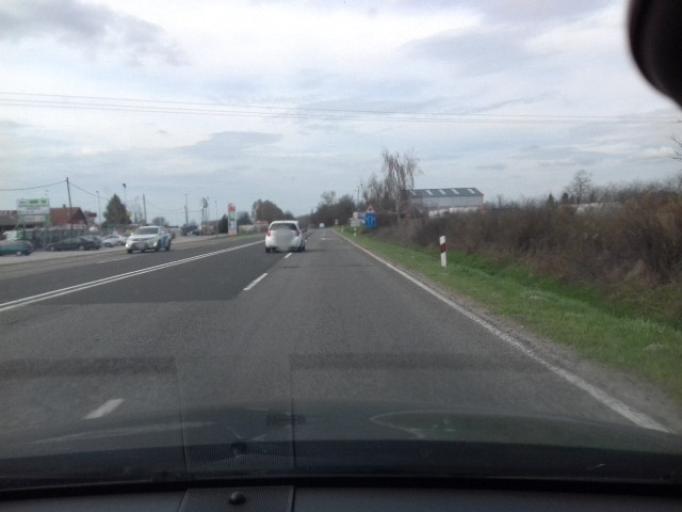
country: HU
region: Bacs-Kiskun
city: Kecskemet
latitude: 46.9593
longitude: 19.6450
